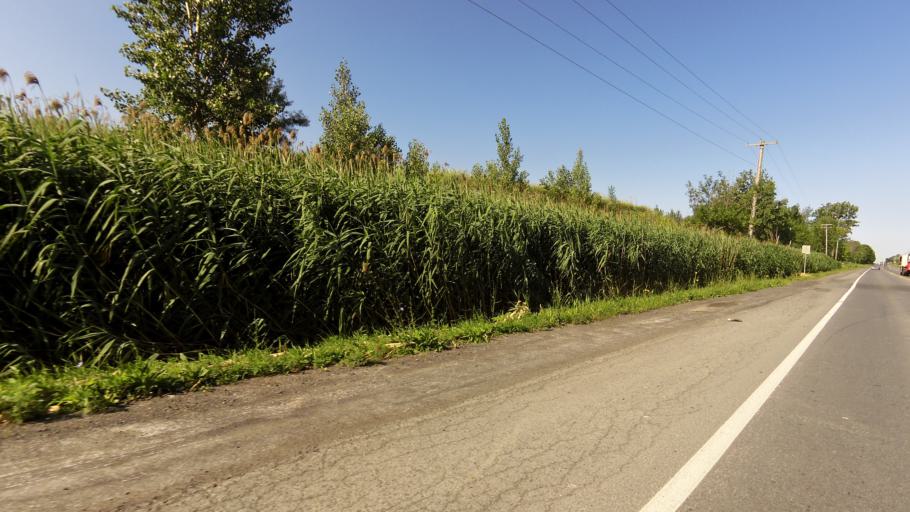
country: CA
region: Quebec
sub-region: Monteregie
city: Saint-Jean-sur-Richelieu
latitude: 45.3035
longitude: -73.2972
